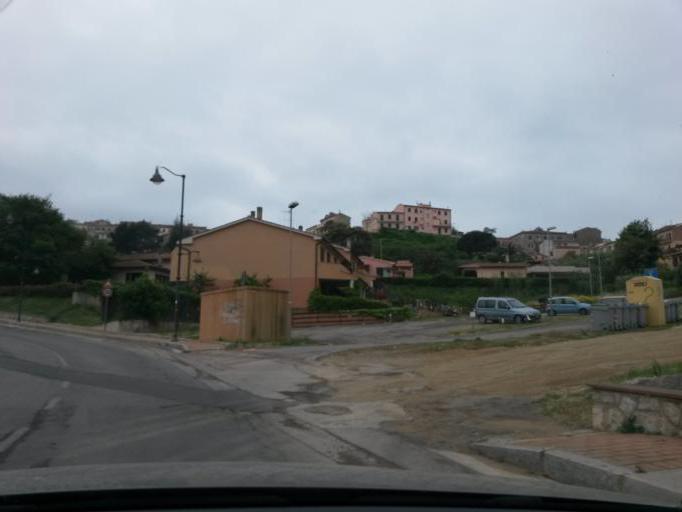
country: IT
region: Tuscany
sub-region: Provincia di Livorno
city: Capoliveri
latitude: 42.7467
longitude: 10.3817
